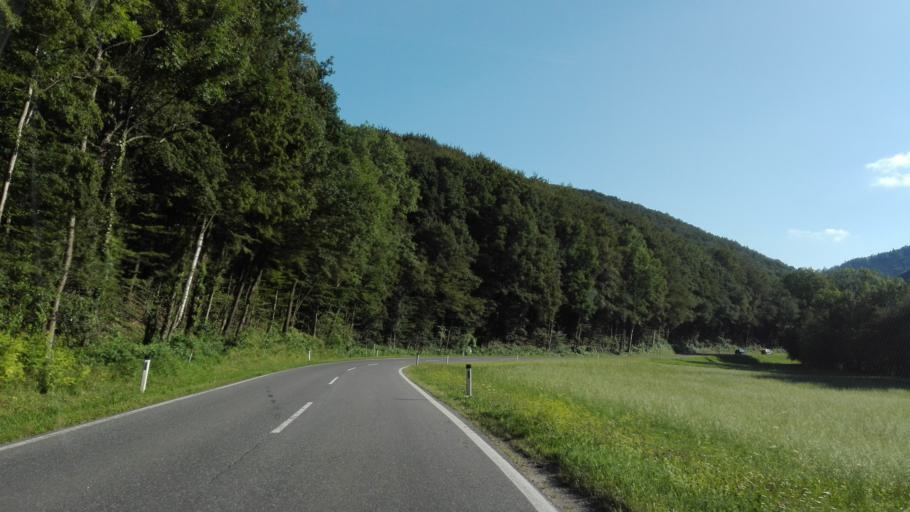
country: AT
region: Lower Austria
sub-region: Politischer Bezirk Sankt Polten
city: Stossing
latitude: 48.0906
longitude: 15.8713
